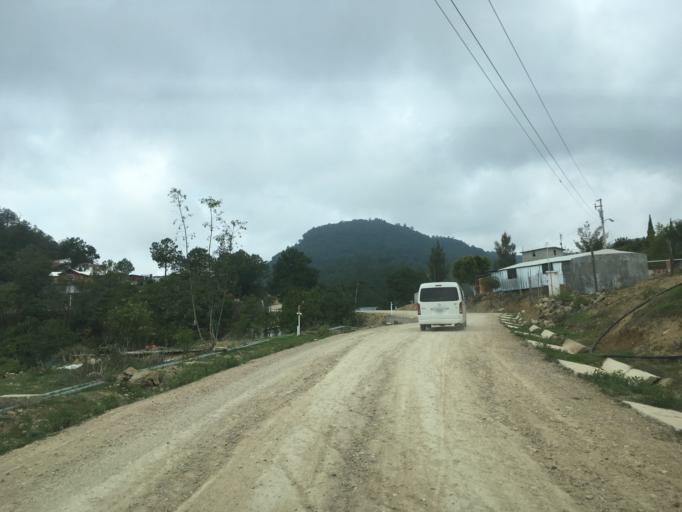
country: MX
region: Oaxaca
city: Santiago Tilantongo
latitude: 17.1973
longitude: -97.2832
